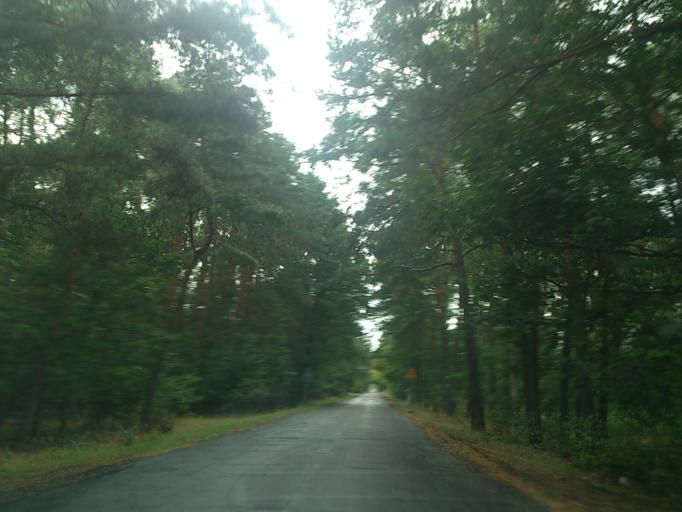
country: PL
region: Greater Poland Voivodeship
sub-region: Powiat poznanski
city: Kobylnica
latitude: 52.5191
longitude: 17.1583
